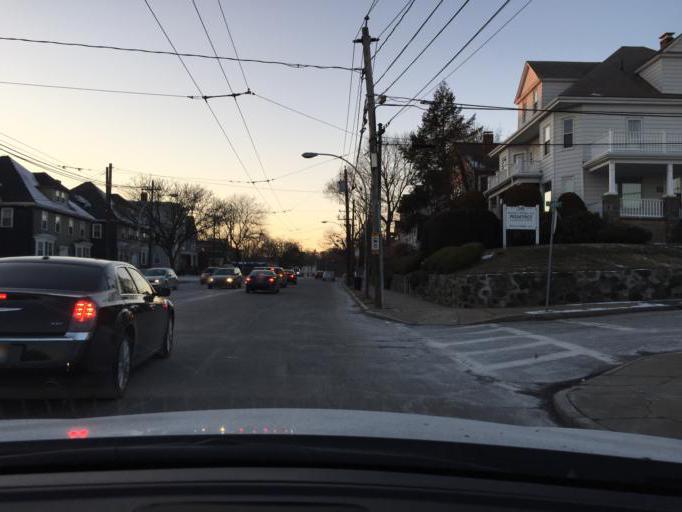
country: US
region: Massachusetts
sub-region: Middlesex County
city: Watertown
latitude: 42.3704
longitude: -71.1602
